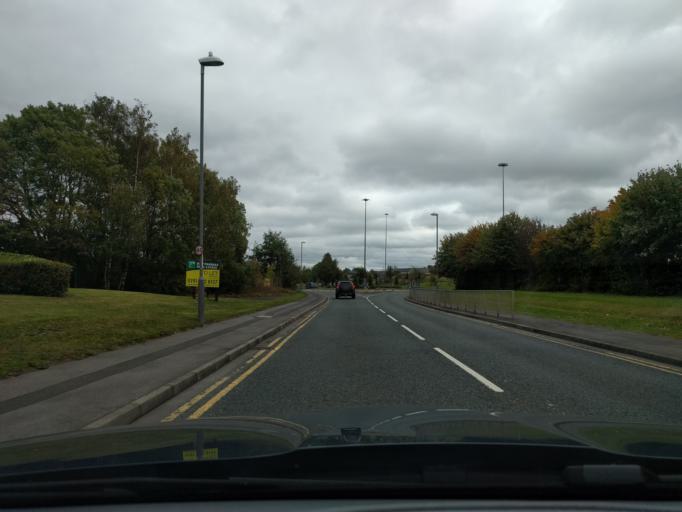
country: GB
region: England
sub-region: Newcastle upon Tyne
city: Benwell
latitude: 54.9603
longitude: -1.6665
